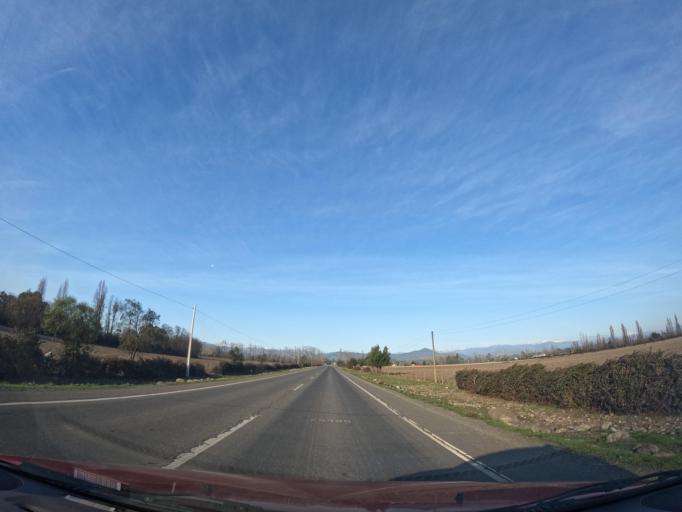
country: CL
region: Maule
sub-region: Provincia de Linares
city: Colbun
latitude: -35.6301
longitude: -71.4407
